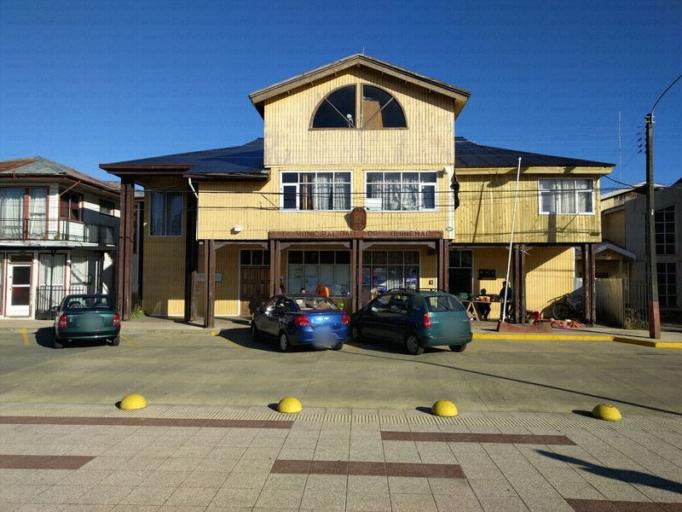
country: CL
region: Los Lagos
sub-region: Provincia de Chiloe
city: Castro
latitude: -42.4711
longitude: -73.4882
